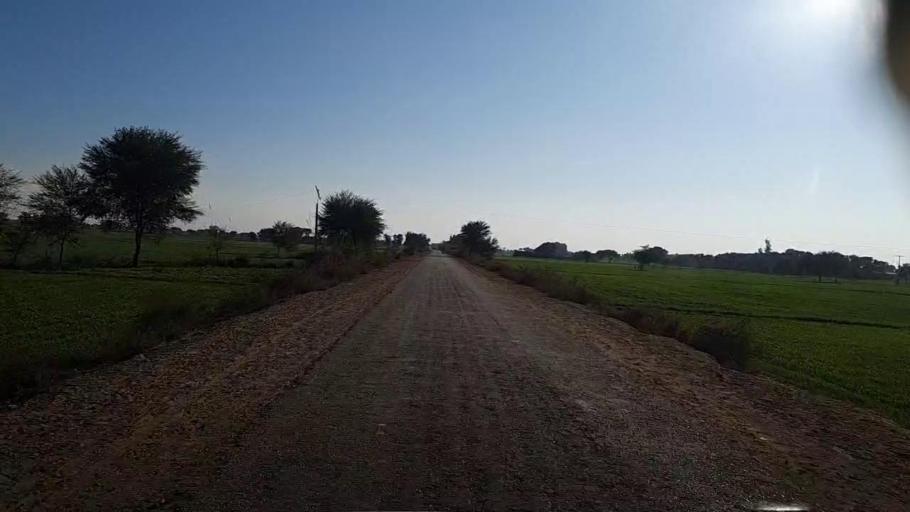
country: PK
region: Sindh
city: Khairpur
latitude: 27.8978
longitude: 69.7476
